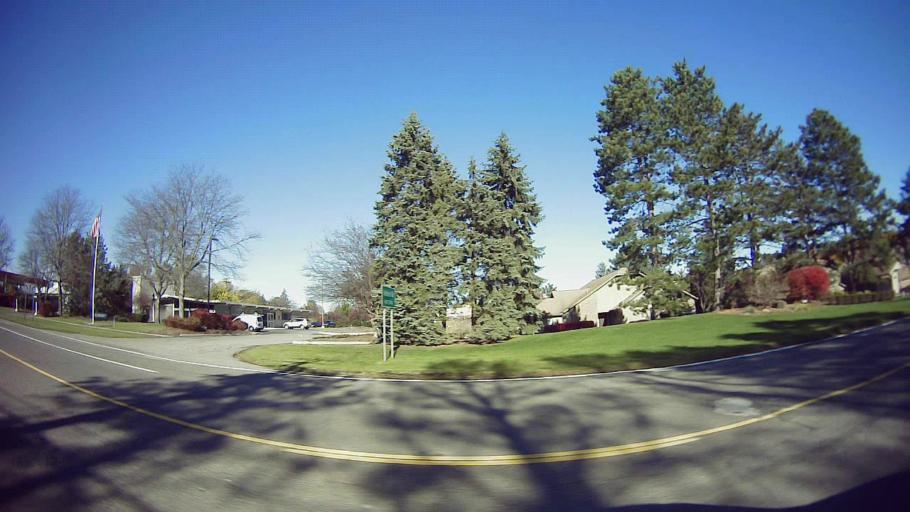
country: US
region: Michigan
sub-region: Oakland County
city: Franklin
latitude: 42.5439
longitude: -83.3197
